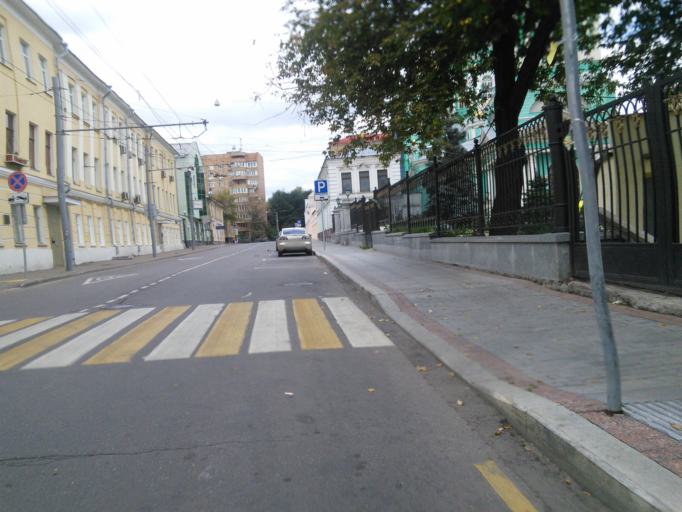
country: RU
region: Moscow
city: Lefortovo
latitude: 55.7722
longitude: 37.6732
